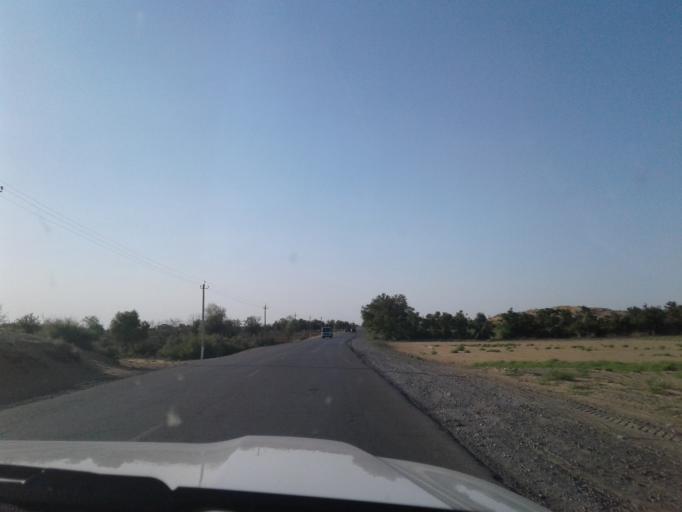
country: TM
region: Mary
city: Yoloeten
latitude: 37.2214
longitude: 62.3763
